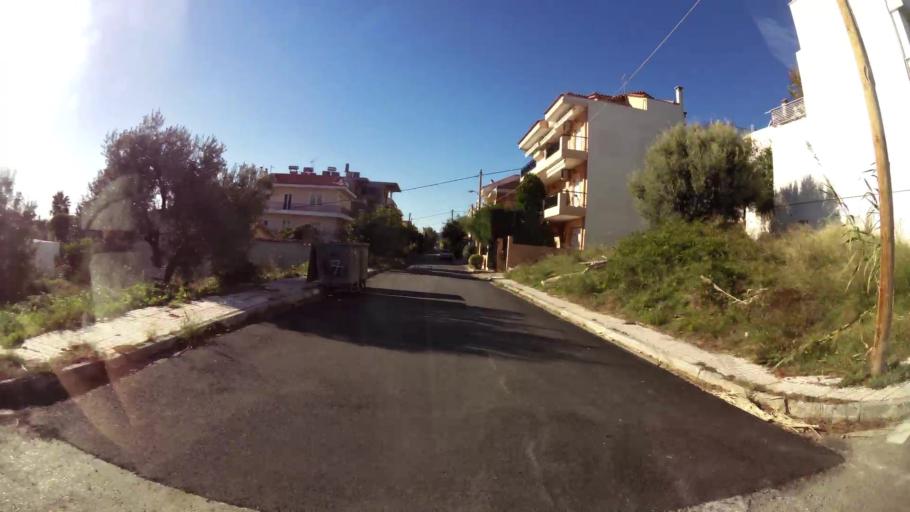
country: GR
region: Attica
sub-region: Nomarchia Anatolikis Attikis
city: Gerakas
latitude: 38.0160
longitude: 23.8493
